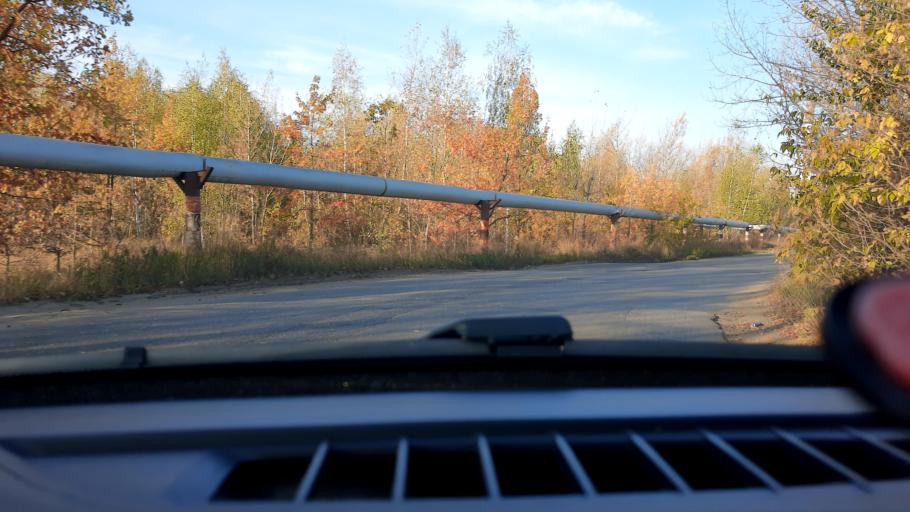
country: RU
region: Nizjnij Novgorod
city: Neklyudovo
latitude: 56.3496
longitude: 43.9034
